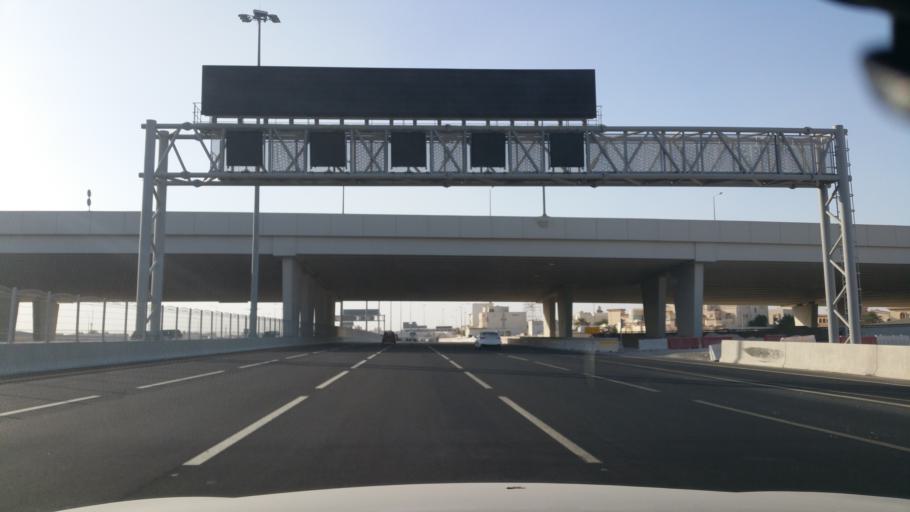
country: QA
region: Baladiyat ad Dawhah
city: Doha
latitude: 25.2370
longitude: 51.5234
